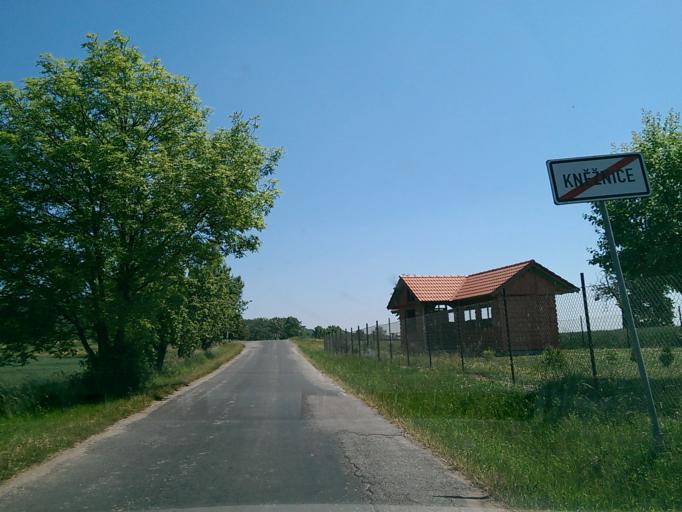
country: CZ
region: Liberecky
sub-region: Okres Semily
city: Lomnice nad Popelkou
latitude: 50.4994
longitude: 15.3307
